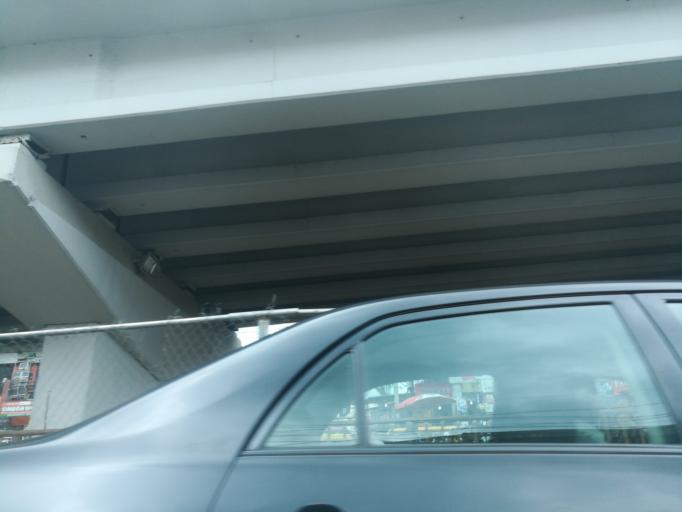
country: NG
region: Lagos
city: Ikeja
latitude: 6.5963
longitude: 3.3414
